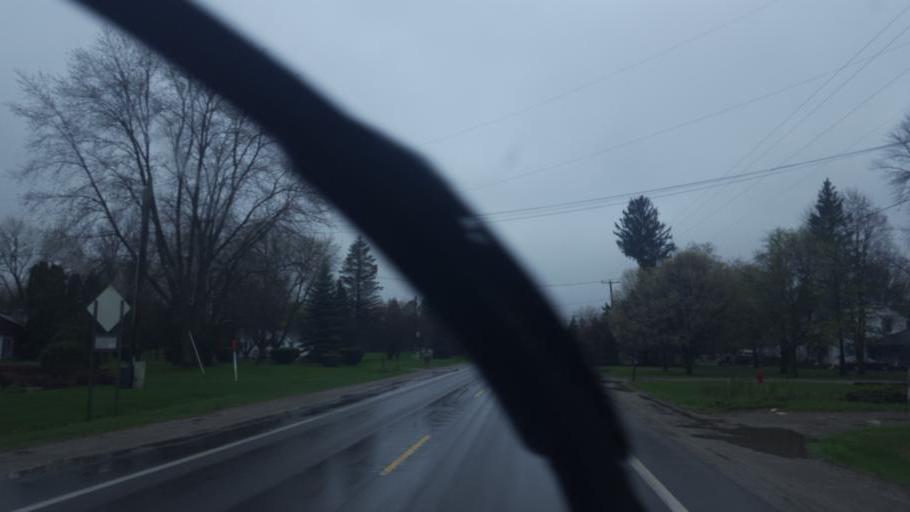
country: US
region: Michigan
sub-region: Isabella County
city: Mount Pleasant
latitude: 43.5969
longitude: -84.8290
